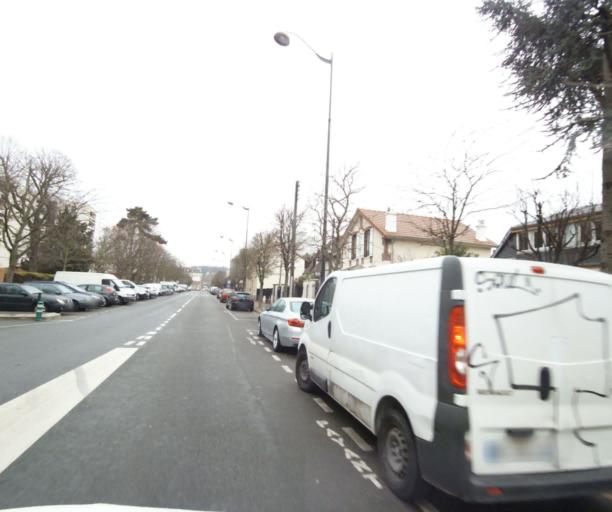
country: FR
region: Ile-de-France
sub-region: Departement des Hauts-de-Seine
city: Rueil-Malmaison
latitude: 48.8869
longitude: 2.1869
